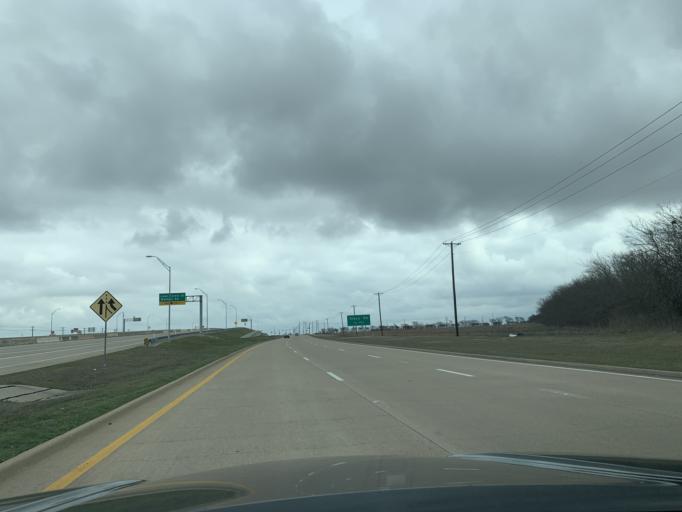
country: US
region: Texas
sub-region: Collin County
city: Allen
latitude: 33.1376
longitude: -96.6966
